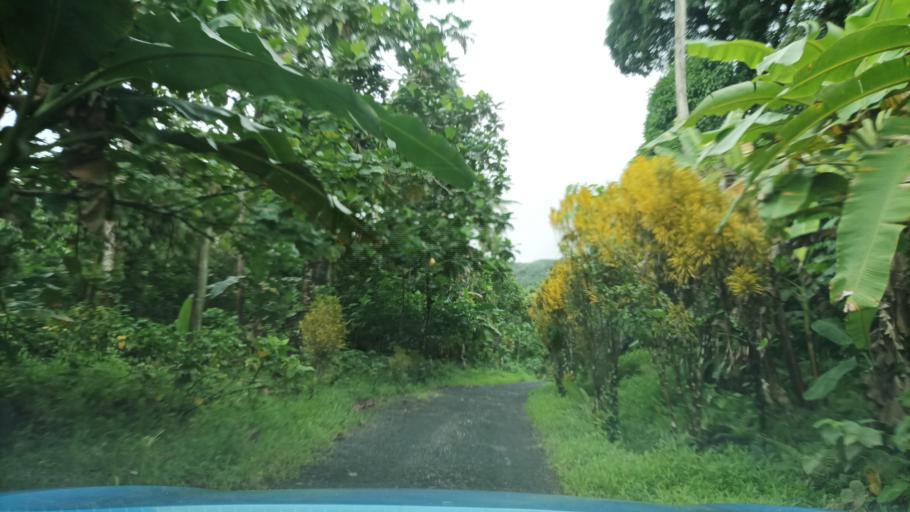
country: FM
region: Pohnpei
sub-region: Kolonia Municipality
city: Kolonia
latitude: 6.9202
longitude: 158.2752
